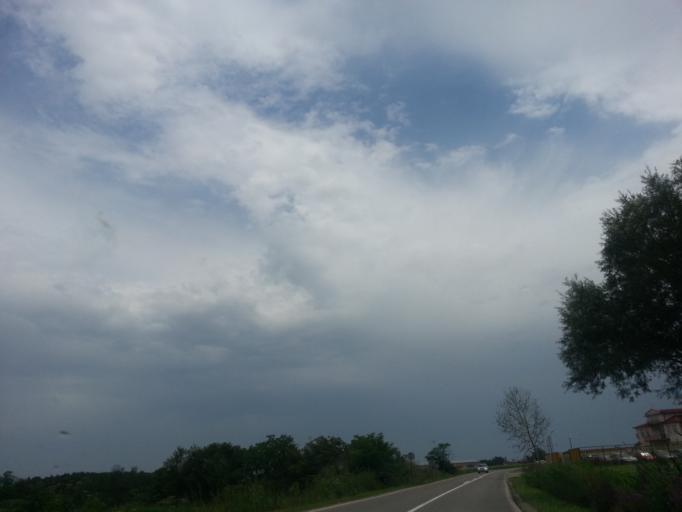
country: BA
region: Republika Srpska
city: Velika Obarska
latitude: 44.7698
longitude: 19.1449
